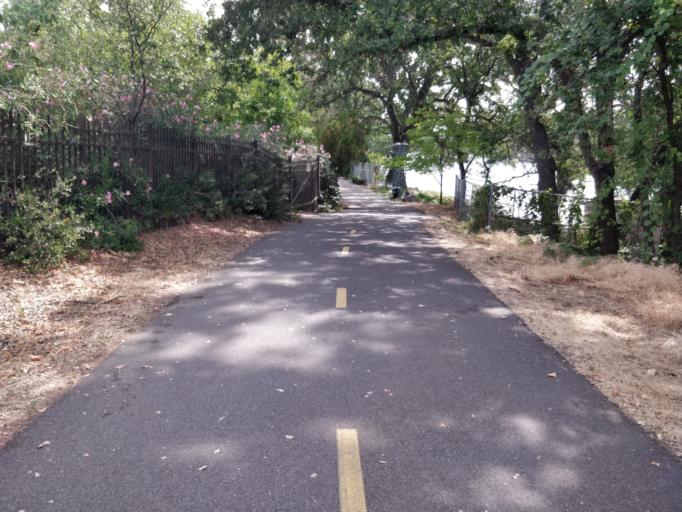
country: US
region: California
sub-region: Shasta County
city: Redding
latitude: 40.5940
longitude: -122.4055
